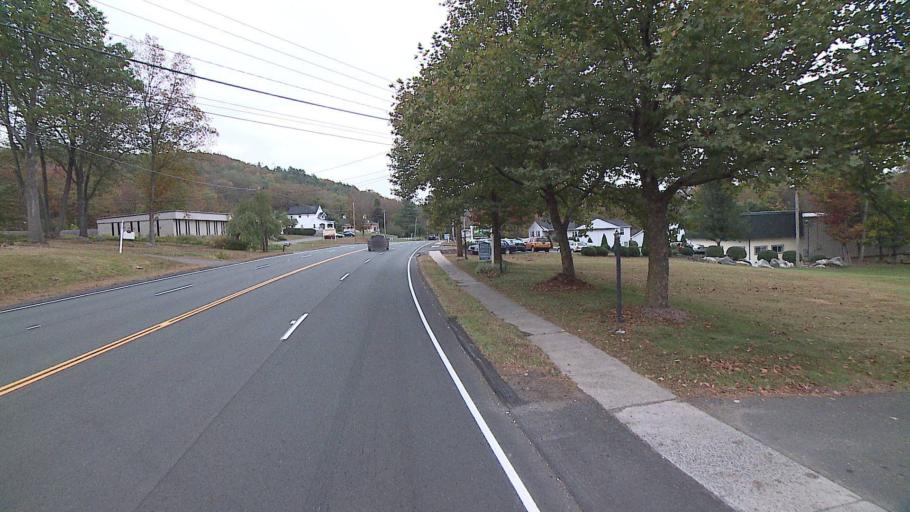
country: US
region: Connecticut
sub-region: Hartford County
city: Canton Valley
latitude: 41.8308
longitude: -72.9058
